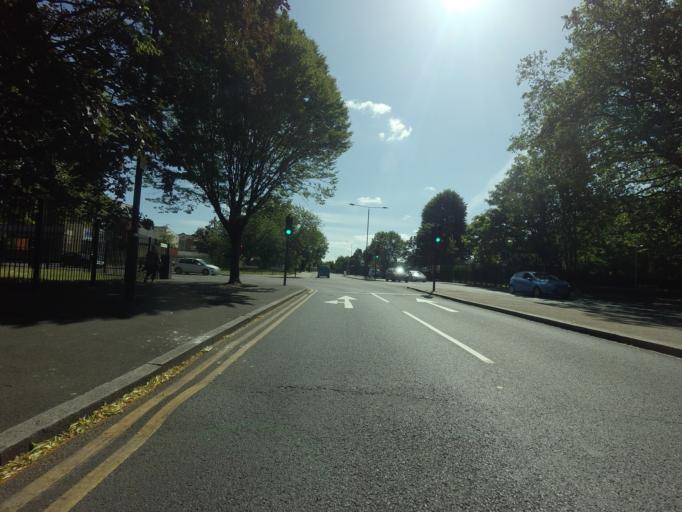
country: GB
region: England
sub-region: Greater London
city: Poplar
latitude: 51.5372
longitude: 0.0091
